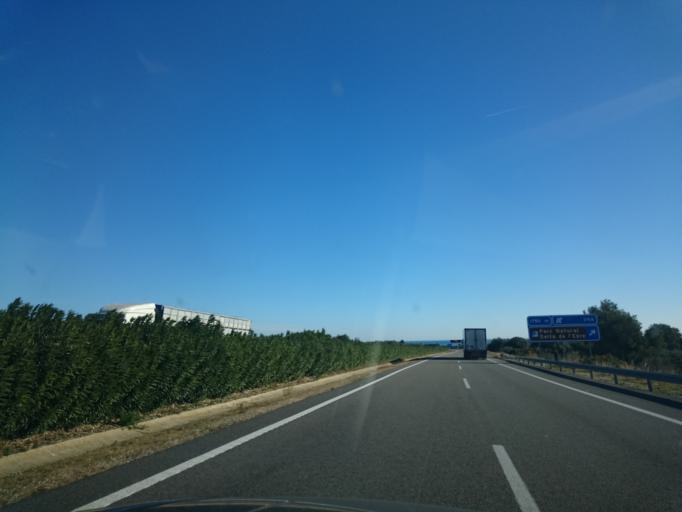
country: ES
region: Catalonia
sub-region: Provincia de Tarragona
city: L'Ampolla
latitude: 40.8028
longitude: 0.6819
